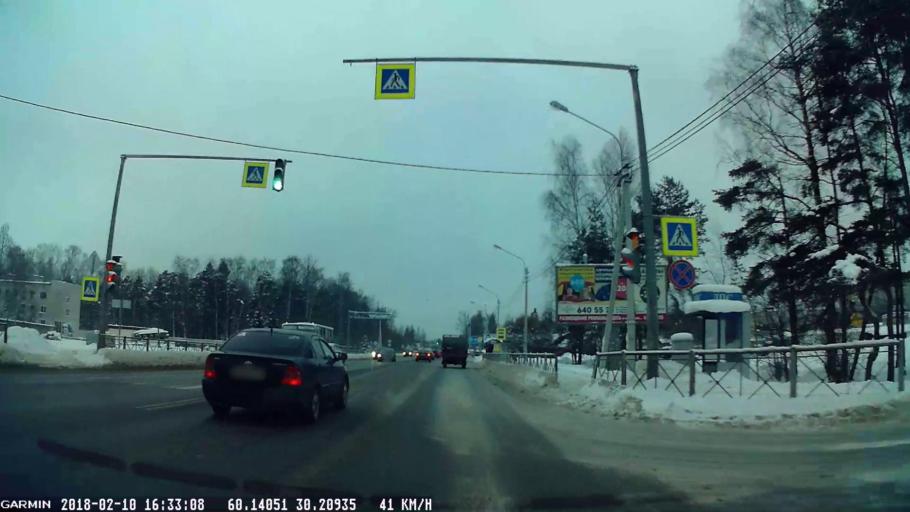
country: RU
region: Leningrad
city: Sertolovo
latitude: 60.1411
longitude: 30.2086
